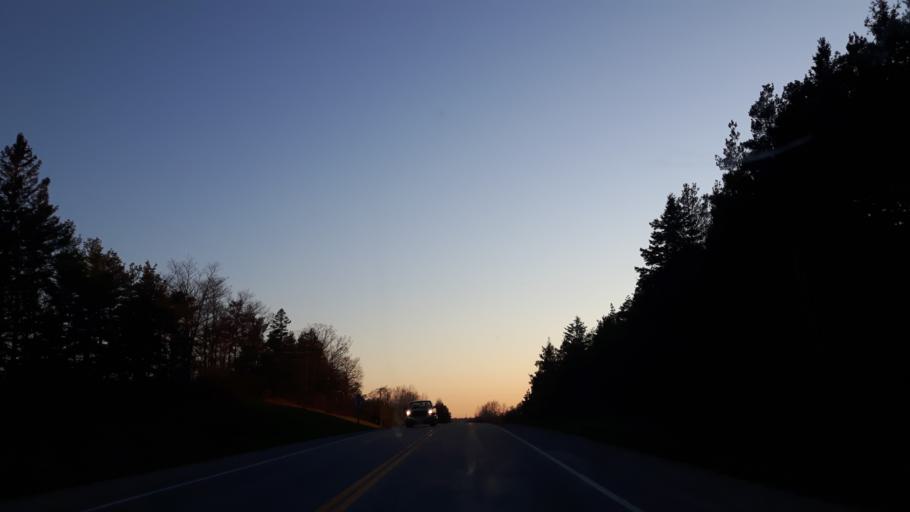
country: CA
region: Ontario
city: Bluewater
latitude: 43.5943
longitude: -81.5643
